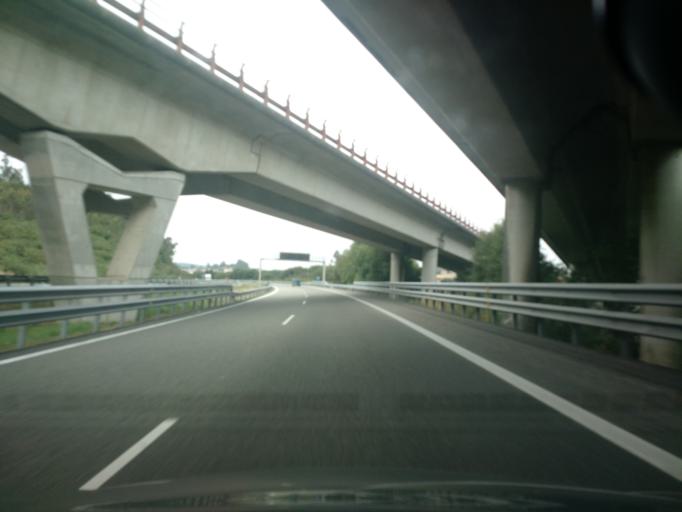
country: ES
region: Galicia
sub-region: Provincia da Coruna
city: Santiago de Compostela
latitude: 42.9008
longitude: -8.5000
